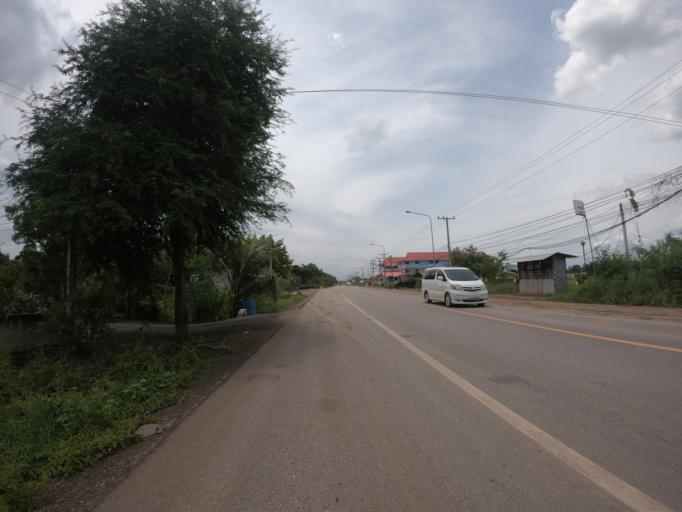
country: TH
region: Pathum Thani
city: Nong Suea
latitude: 14.0472
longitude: 100.8704
